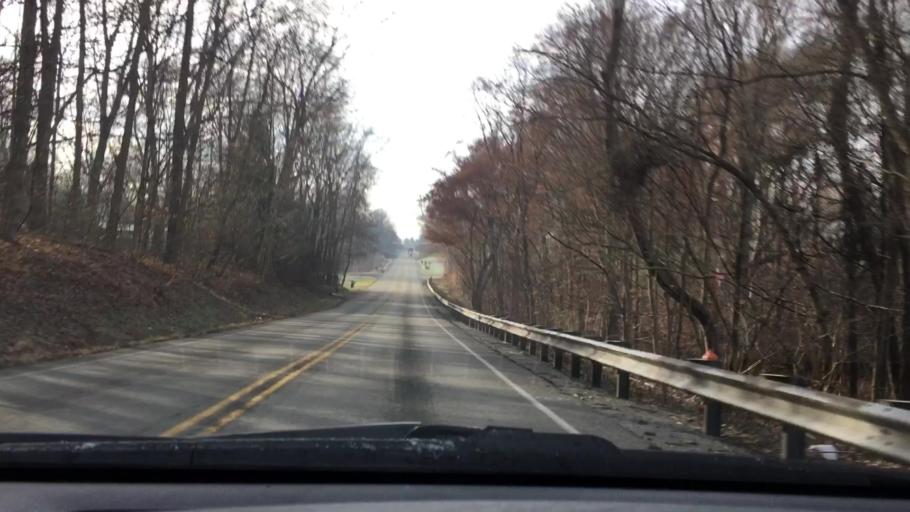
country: US
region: Pennsylvania
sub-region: Allegheny County
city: Industry
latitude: 40.2634
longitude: -79.7681
